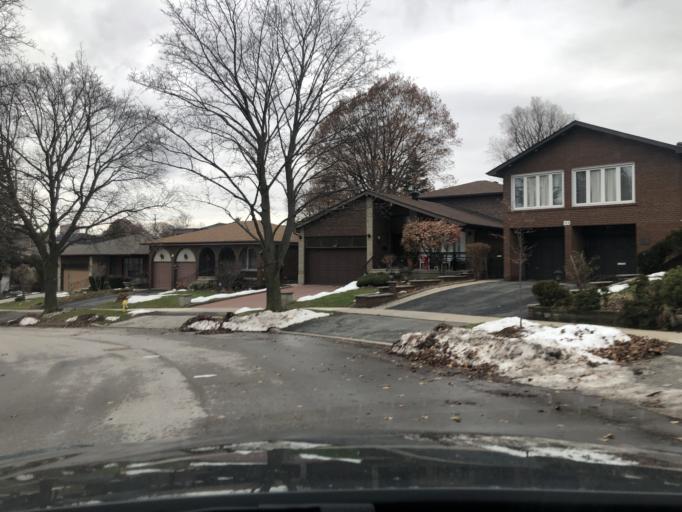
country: CA
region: Ontario
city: Etobicoke
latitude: 43.6945
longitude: -79.5304
